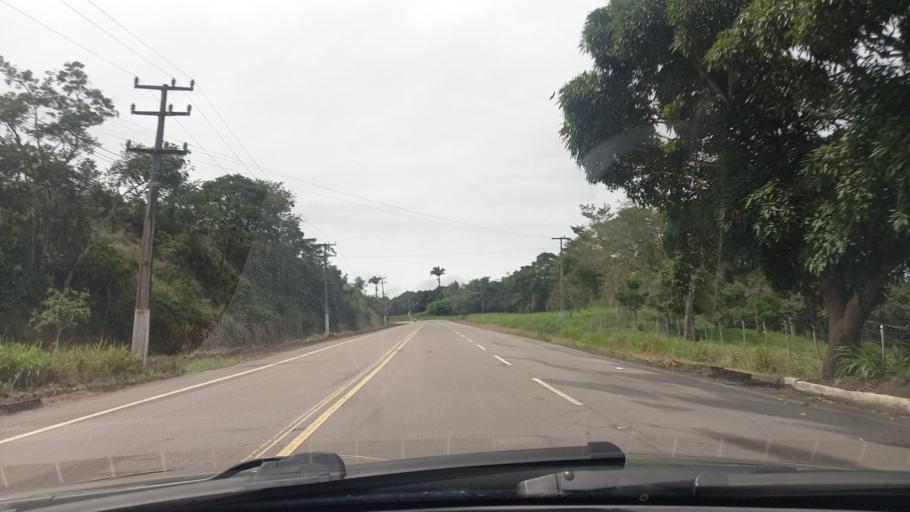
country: BR
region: Alagoas
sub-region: Sao Miguel Dos Campos
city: Sao Miguel dos Campos
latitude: -9.8091
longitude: -36.2145
